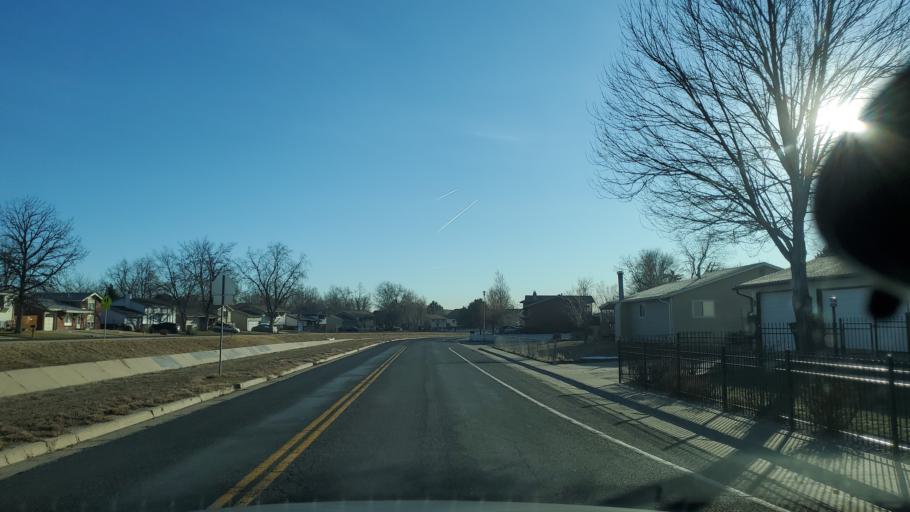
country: US
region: Colorado
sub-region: Adams County
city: Welby
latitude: 39.8444
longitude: -104.9716
